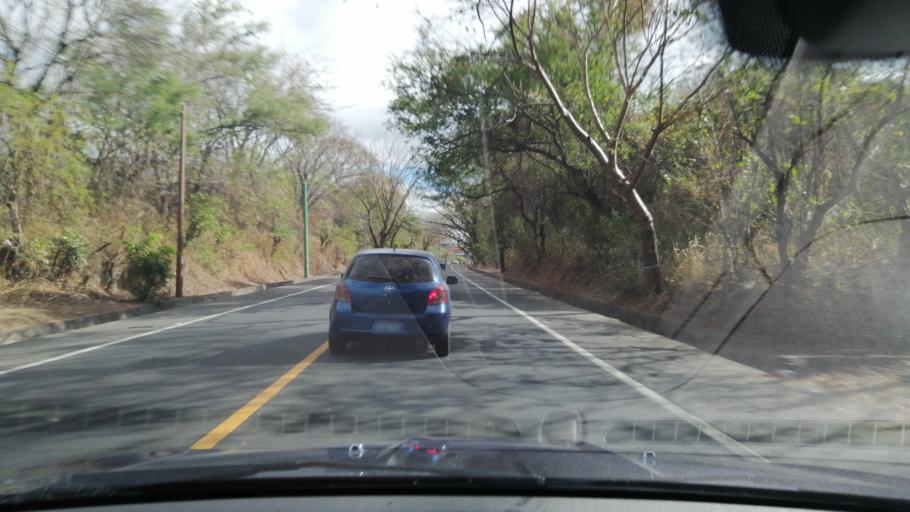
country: SV
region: Santa Ana
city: Santa Ana
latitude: 14.0089
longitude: -89.5426
